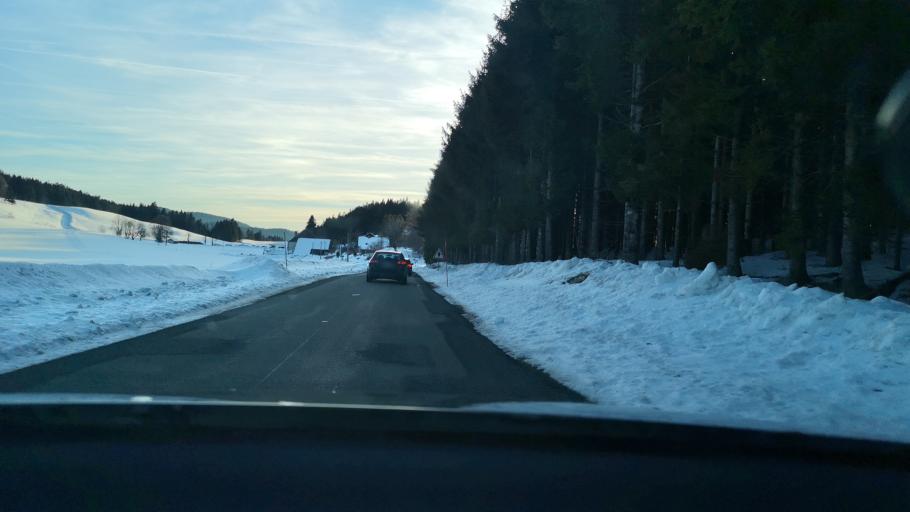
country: FR
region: Franche-Comte
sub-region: Departement du Doubs
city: Gilley
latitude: 46.9674
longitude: 6.4765
